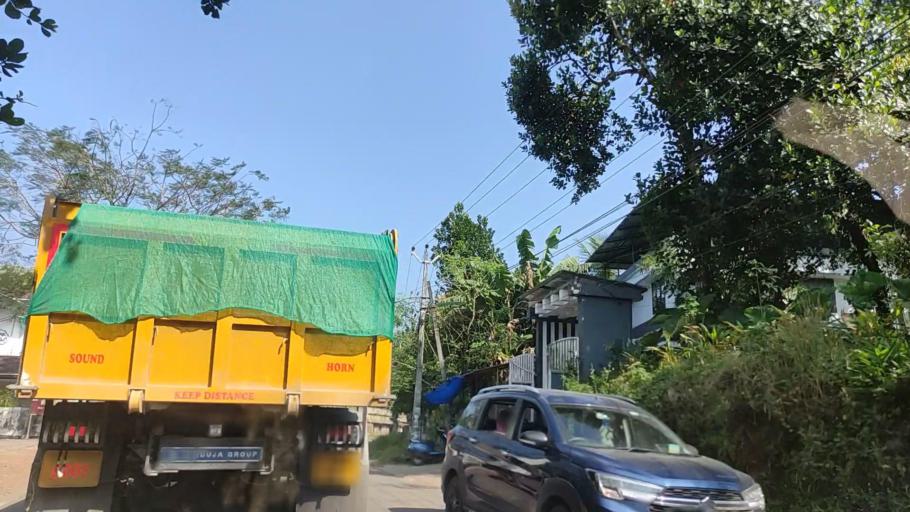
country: IN
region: Kerala
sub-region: Kollam
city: Punalur
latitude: 8.9176
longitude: 76.8930
